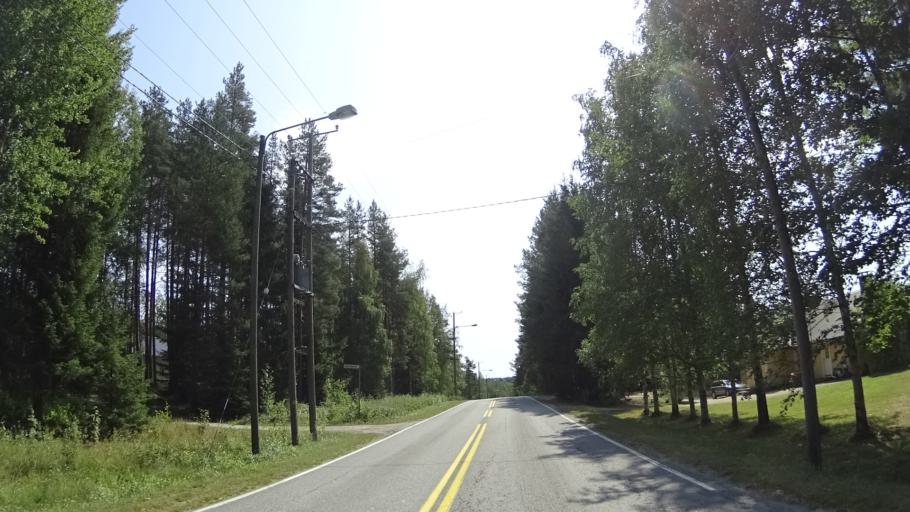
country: FI
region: Pirkanmaa
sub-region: Ylae-Pirkanmaa
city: Maenttae
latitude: 61.9016
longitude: 24.7911
